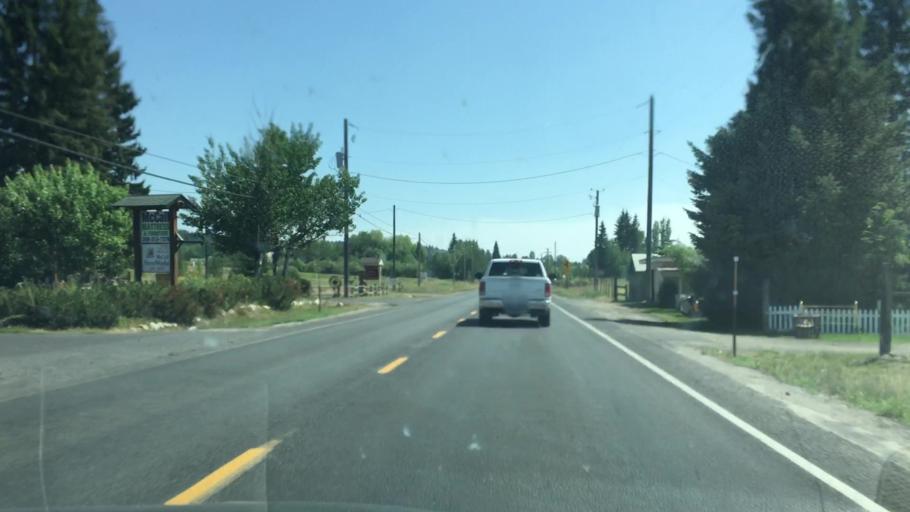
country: US
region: Idaho
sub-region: Valley County
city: McCall
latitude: 44.8928
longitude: -116.0944
